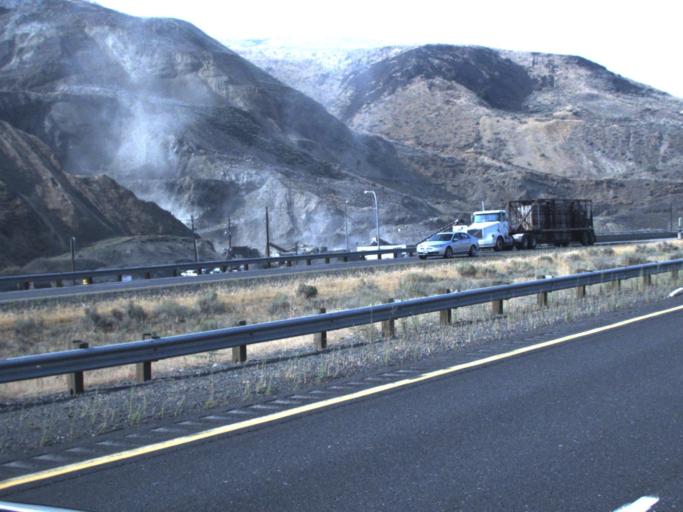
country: US
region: Washington
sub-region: Yakima County
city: Selah
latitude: 46.6477
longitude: -120.5025
